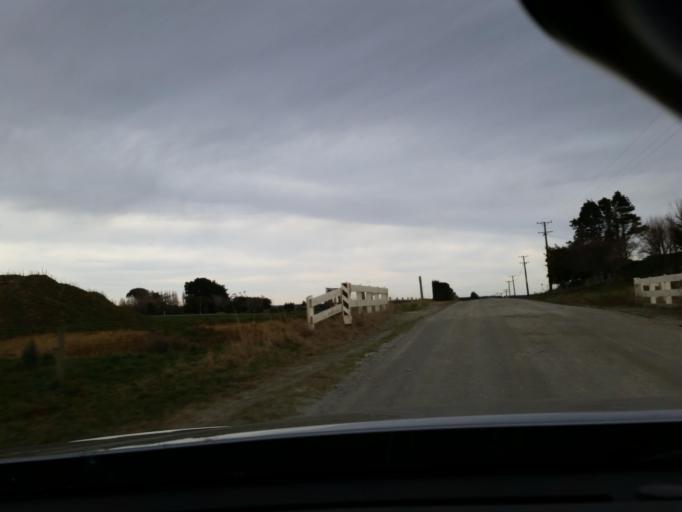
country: NZ
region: Southland
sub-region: Invercargill City
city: Invercargill
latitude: -46.4205
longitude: 168.5061
